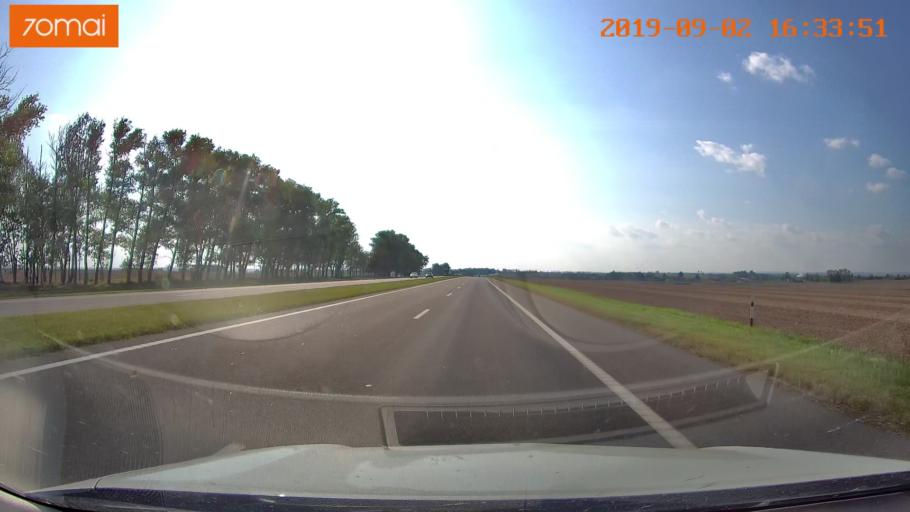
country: BY
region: Minsk
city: Smilavichy
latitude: 53.7606
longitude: 28.0506
